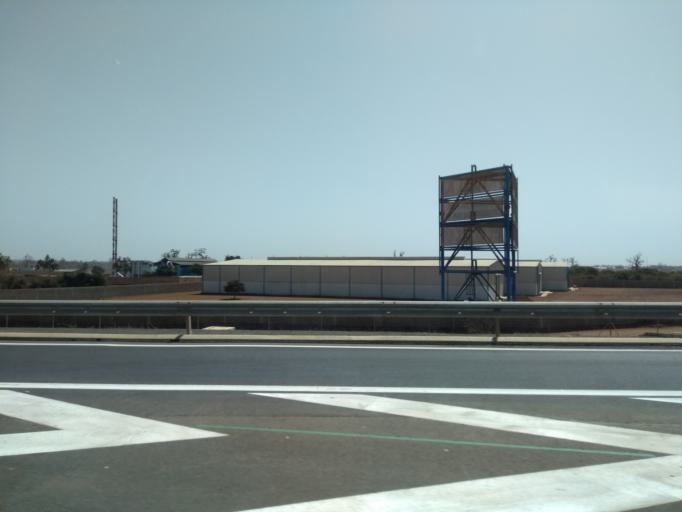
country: SN
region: Thies
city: Pout
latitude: 14.7284
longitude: -17.1560
